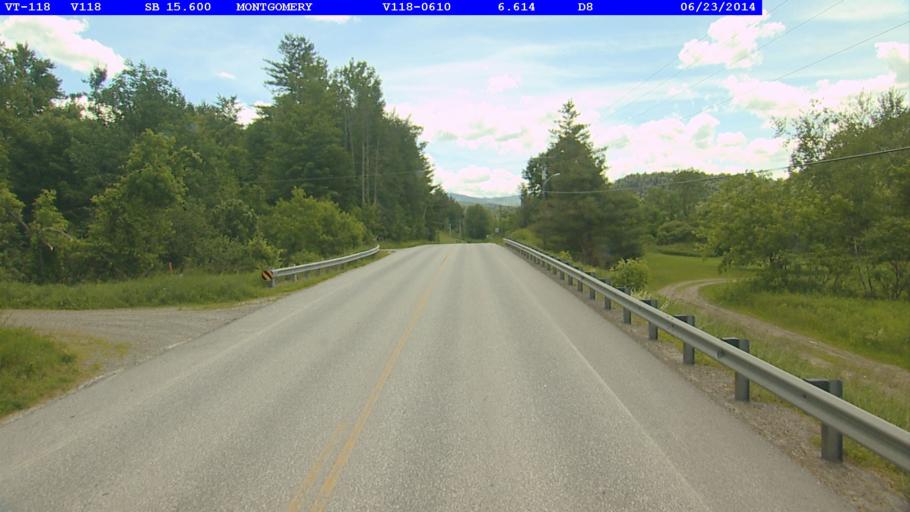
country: US
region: Vermont
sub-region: Franklin County
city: Richford
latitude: 44.8887
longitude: -72.6198
